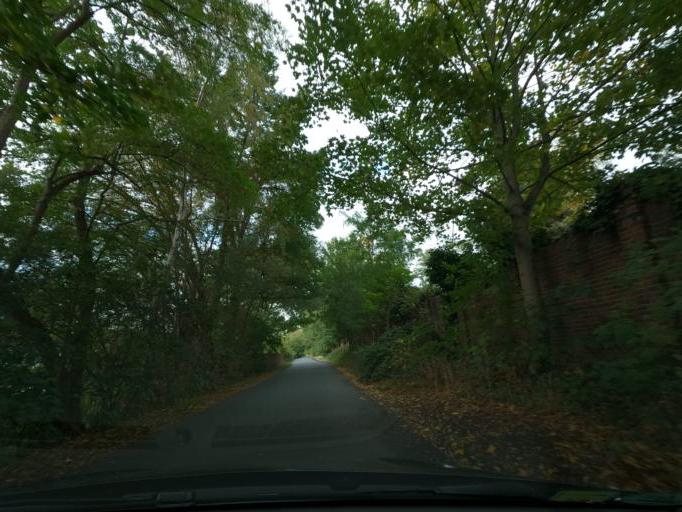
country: DE
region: Lower Saxony
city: Braunschweig
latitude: 52.2438
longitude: 10.5455
